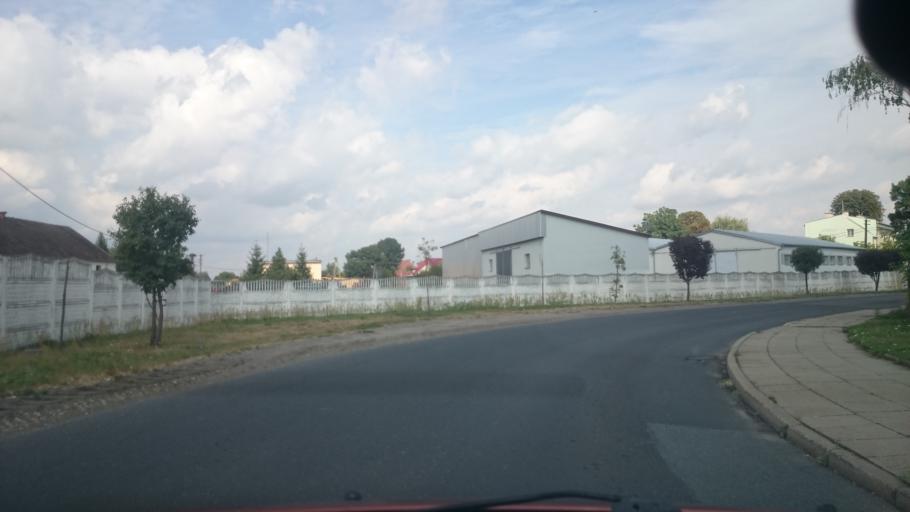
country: PL
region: Opole Voivodeship
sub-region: Powiat nyski
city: Nysa
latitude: 50.4886
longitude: 17.2542
